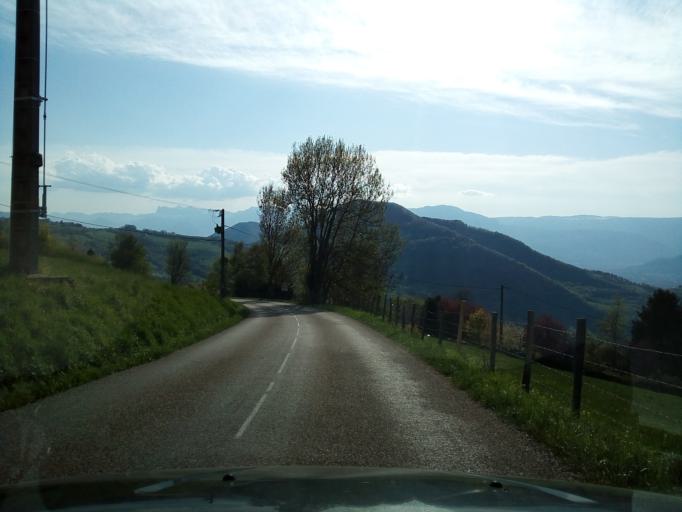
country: FR
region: Rhone-Alpes
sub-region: Departement de l'Isere
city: Revel
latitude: 45.1870
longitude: 5.8799
